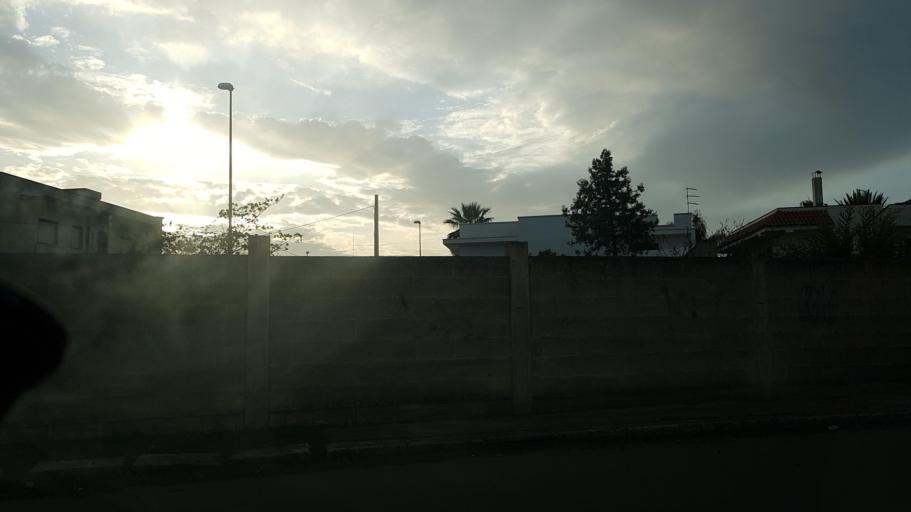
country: IT
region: Apulia
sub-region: Provincia di Brindisi
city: San Pancrazio Salentino
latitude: 40.4130
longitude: 17.8411
